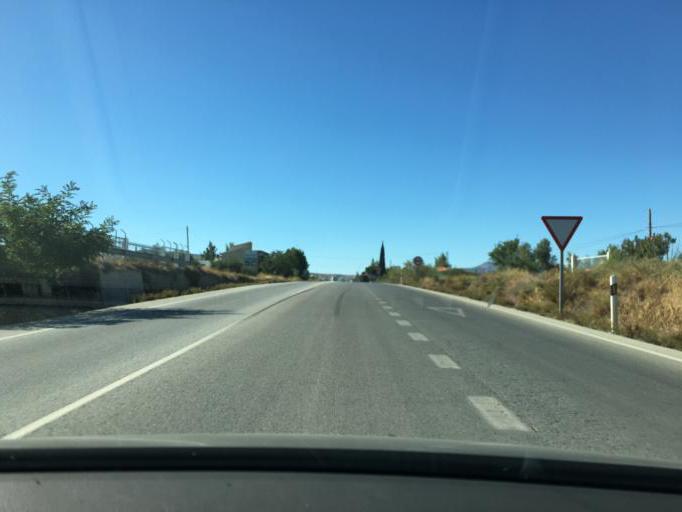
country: ES
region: Andalusia
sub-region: Provincia de Granada
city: Caniles
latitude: 37.4494
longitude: -2.7312
